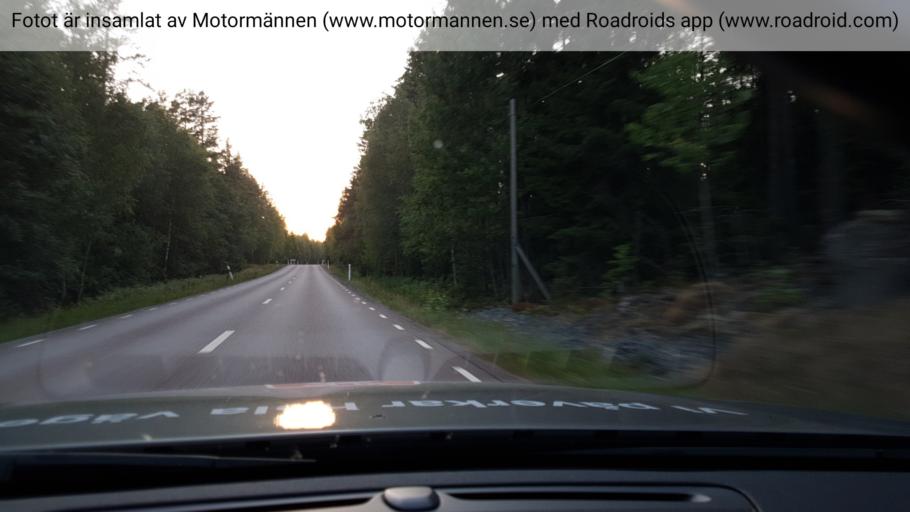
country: SE
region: Uppsala
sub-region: Heby Kommun
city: OEstervala
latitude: 60.0375
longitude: 17.2512
